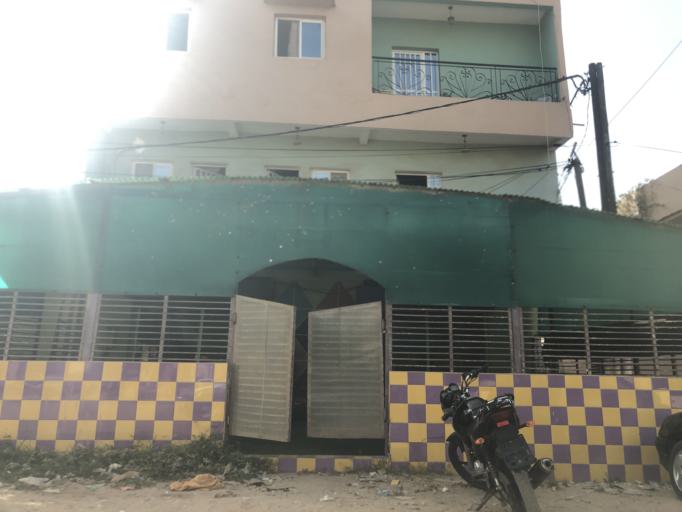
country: SN
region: Dakar
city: Mermoz Boabab
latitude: 14.7321
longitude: -17.4932
